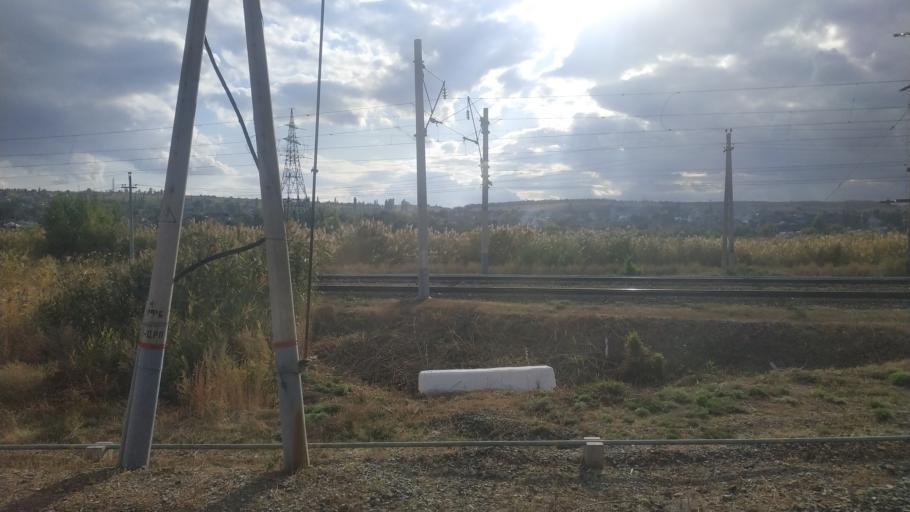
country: RU
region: Volgograd
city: Krasnoslobodsk
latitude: 48.5169
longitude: 44.5166
